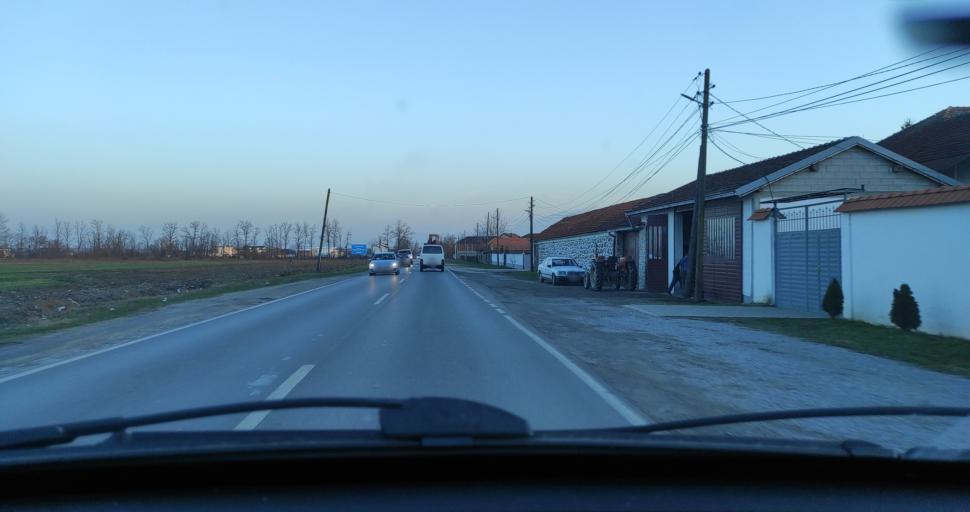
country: XK
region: Gjakova
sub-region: Komuna e Gjakoves
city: Gjakove
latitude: 42.4236
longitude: 20.3911
